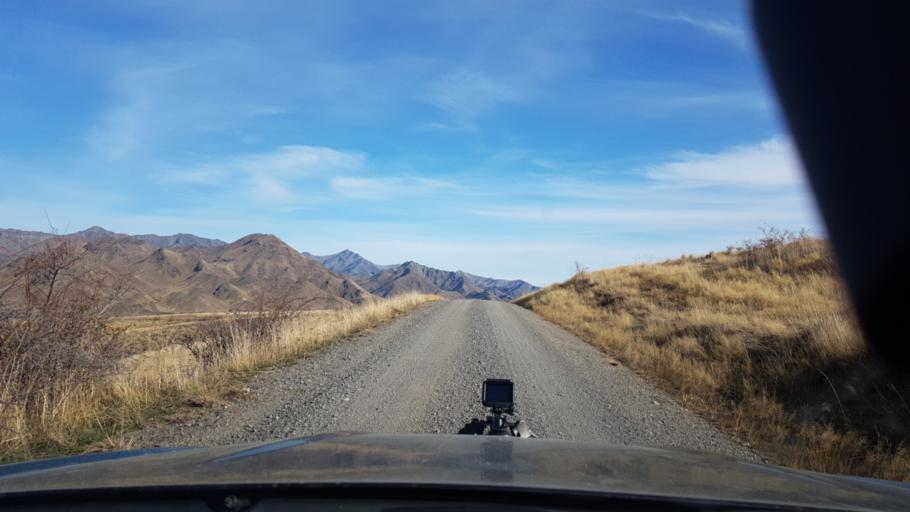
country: NZ
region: Canterbury
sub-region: Kaikoura District
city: Kaikoura
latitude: -42.0462
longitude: 173.3376
